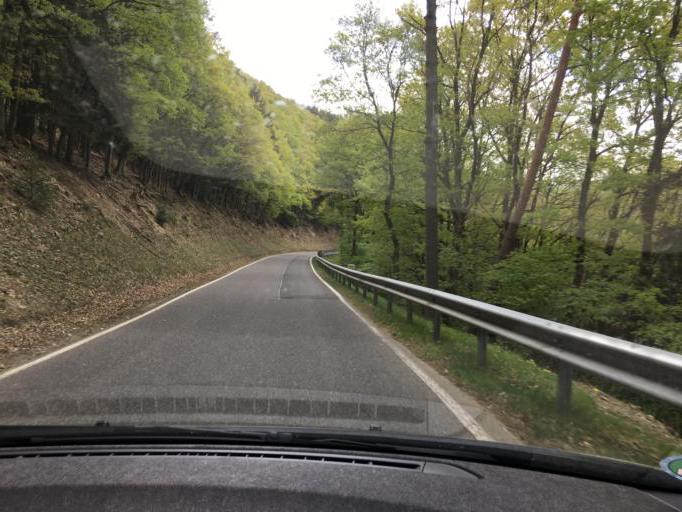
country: DE
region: Rheinland-Pfalz
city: Ahrbruck
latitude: 50.4980
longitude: 6.9561
